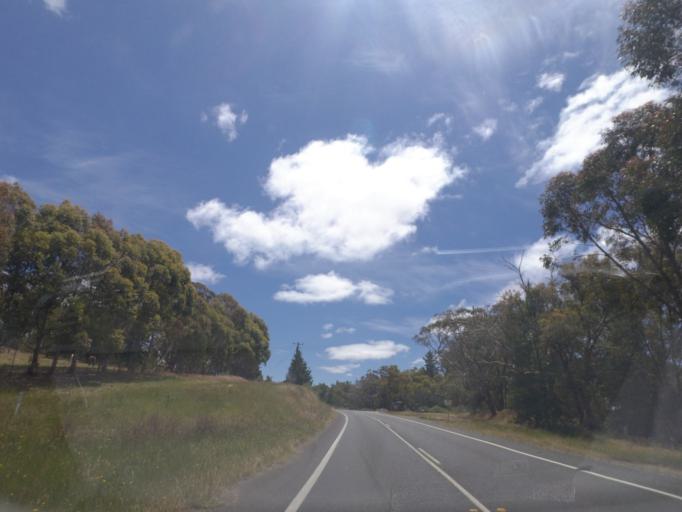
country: AU
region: Victoria
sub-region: Mount Alexander
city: Castlemaine
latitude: -37.2853
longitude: 144.1610
